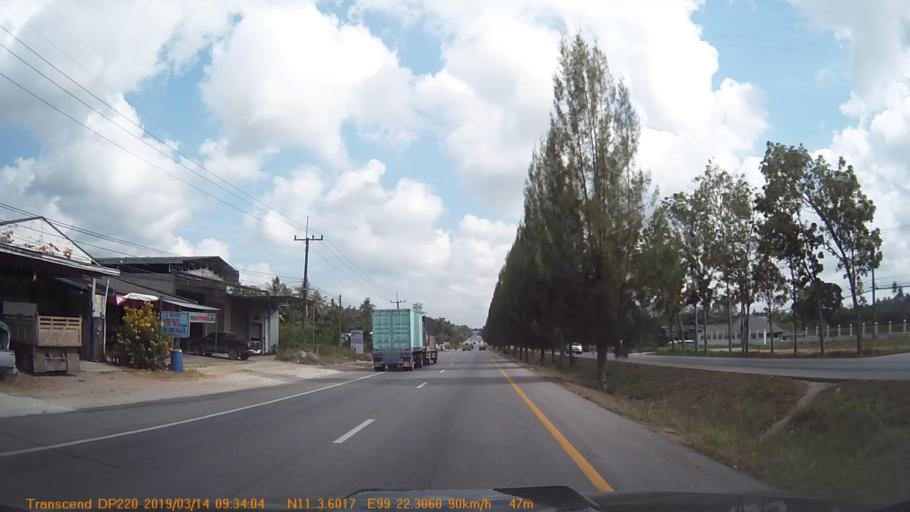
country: TH
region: Prachuap Khiri Khan
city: Bang Saphan Noi
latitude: 11.0609
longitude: 99.3719
